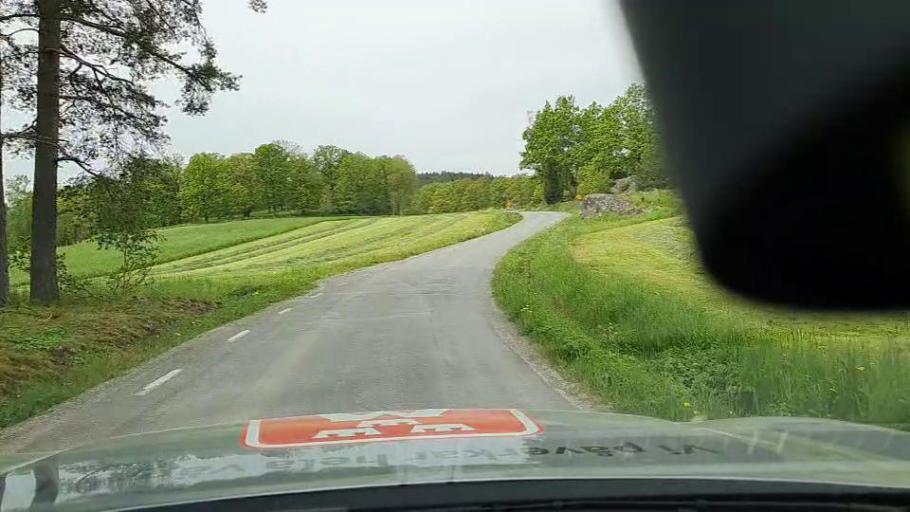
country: SE
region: Soedermanland
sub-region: Flens Kommun
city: Halleforsnas
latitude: 59.1013
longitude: 16.4787
